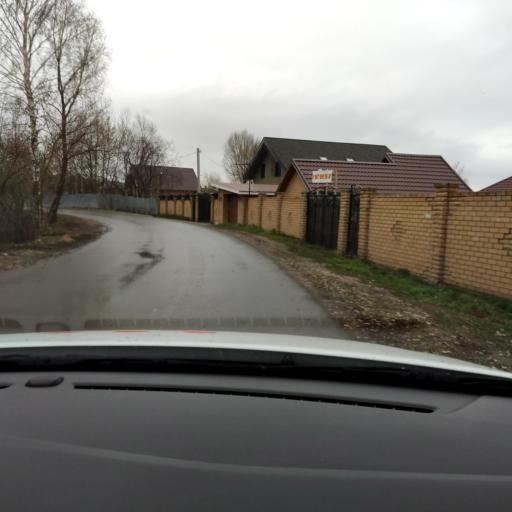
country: RU
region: Tatarstan
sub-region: Gorod Kazan'
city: Kazan
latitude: 55.6921
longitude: 49.0712
